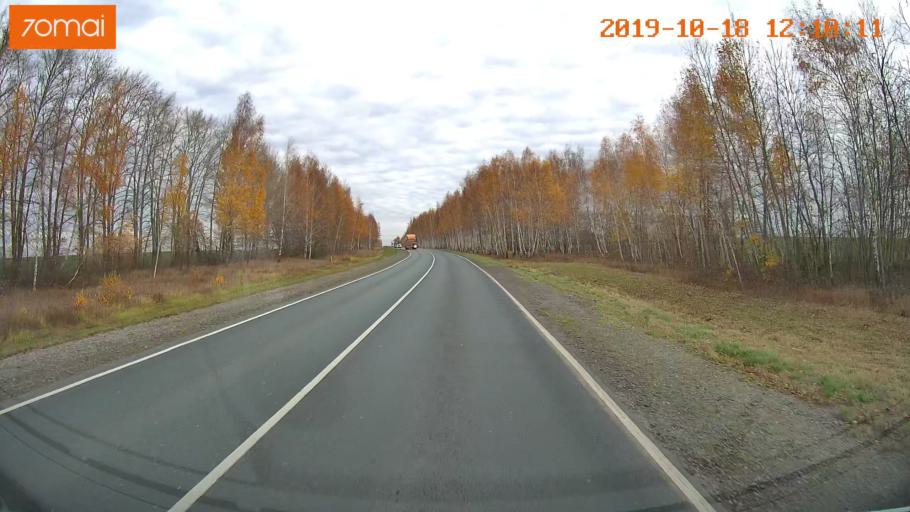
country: RU
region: Rjazan
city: Zakharovo
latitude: 54.3903
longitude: 39.3255
